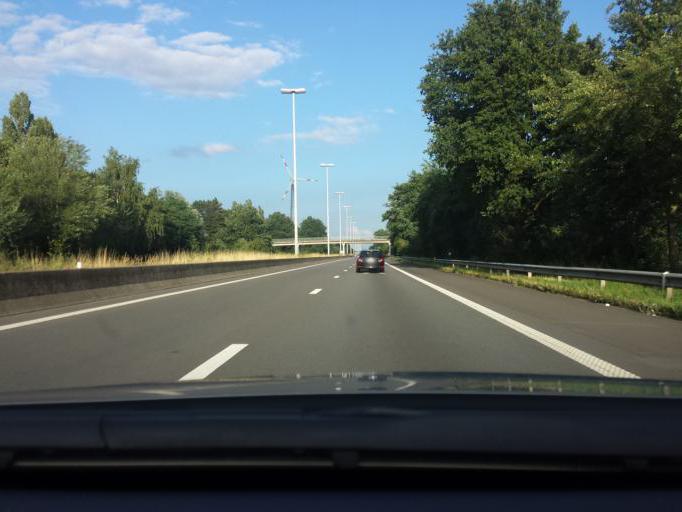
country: BE
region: Flanders
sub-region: Provincie Limburg
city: Tessenderlo
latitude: 51.0956
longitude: 5.0850
